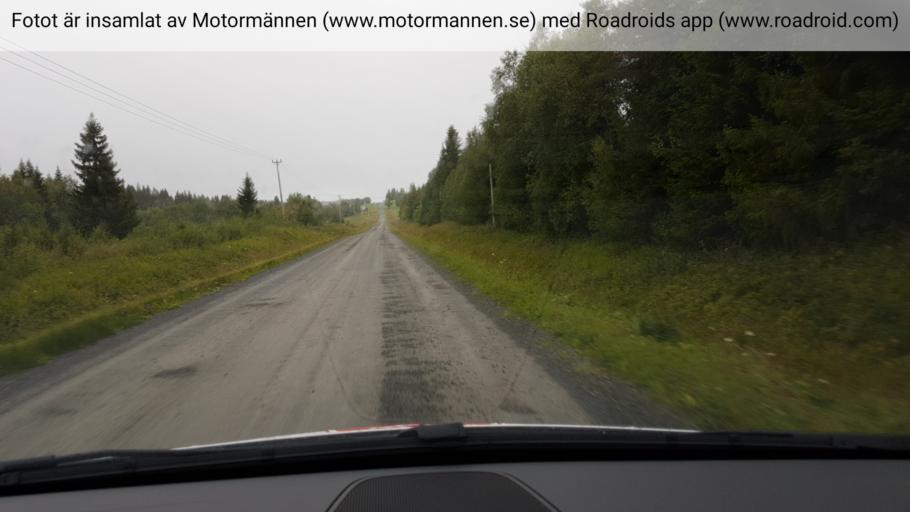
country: SE
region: Jaemtland
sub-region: OEstersunds Kommun
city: Lit
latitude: 63.6345
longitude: 14.9642
